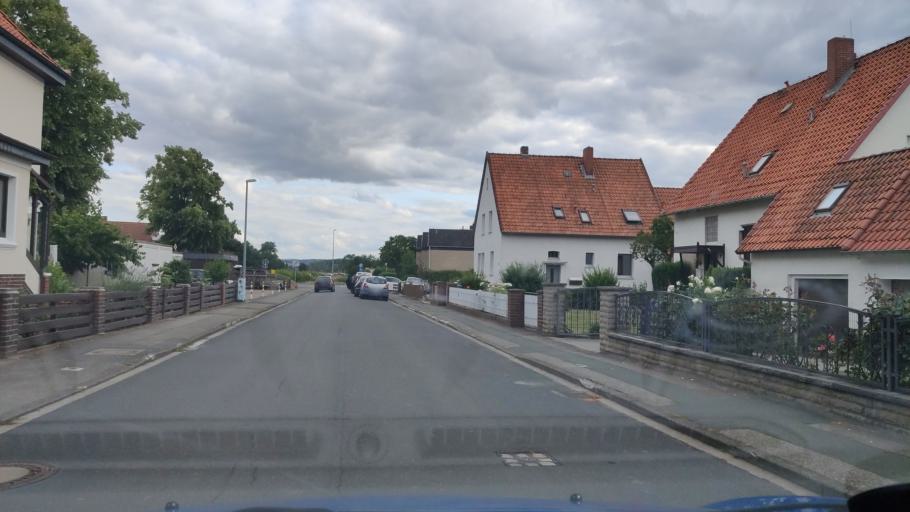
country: DE
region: Lower Saxony
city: Ronnenberg
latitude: 52.2975
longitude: 9.6432
